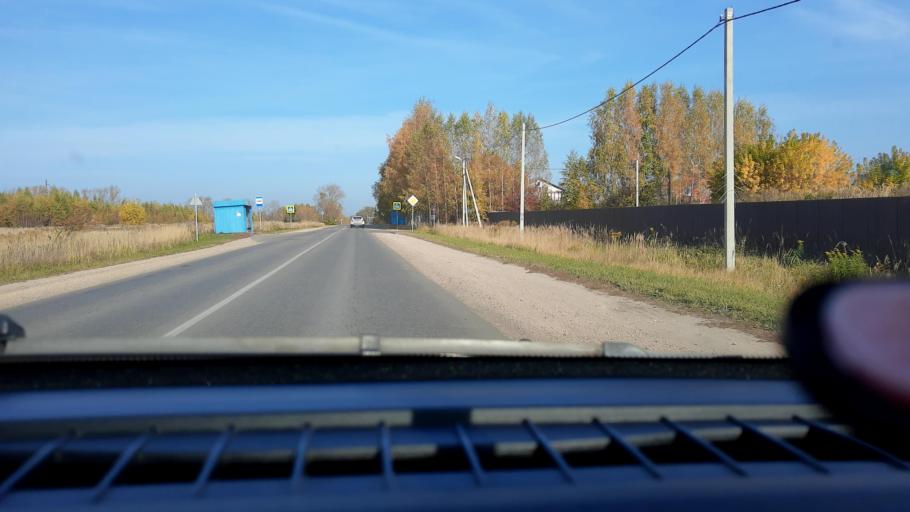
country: RU
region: Nizjnij Novgorod
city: Kstovo
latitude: 56.1482
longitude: 44.2310
